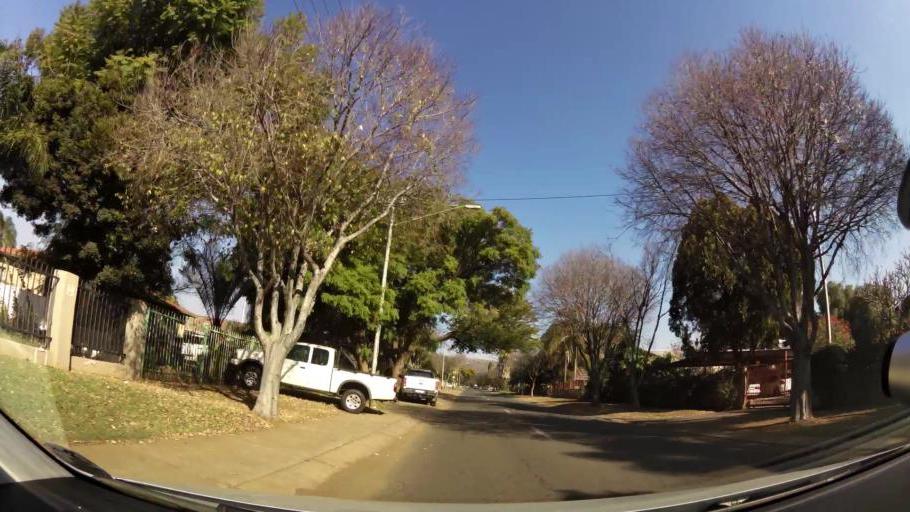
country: ZA
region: Gauteng
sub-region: City of Tshwane Metropolitan Municipality
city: Pretoria
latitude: -25.6650
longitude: 28.1798
